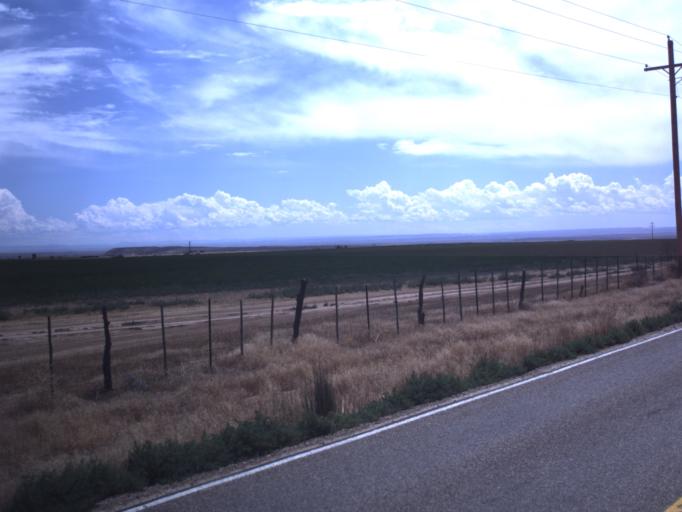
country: US
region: Utah
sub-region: Uintah County
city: Maeser
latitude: 40.2273
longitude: -109.6844
